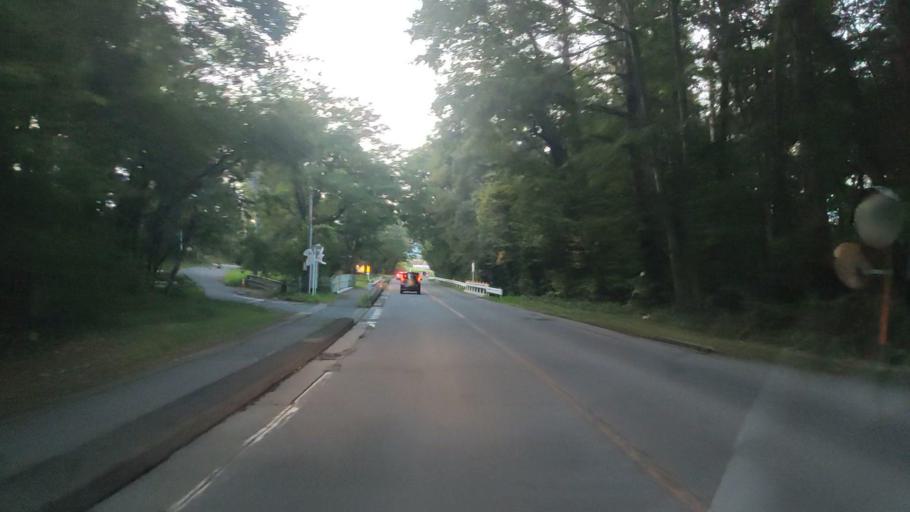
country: JP
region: Nagano
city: Komoro
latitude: 36.4784
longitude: 138.5868
